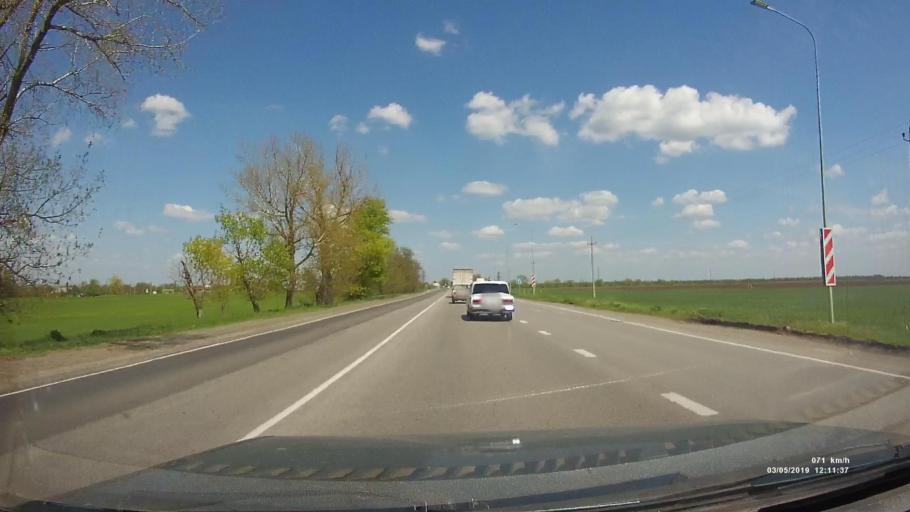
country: RU
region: Rostov
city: Bagayevskaya
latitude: 47.3127
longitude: 40.5400
